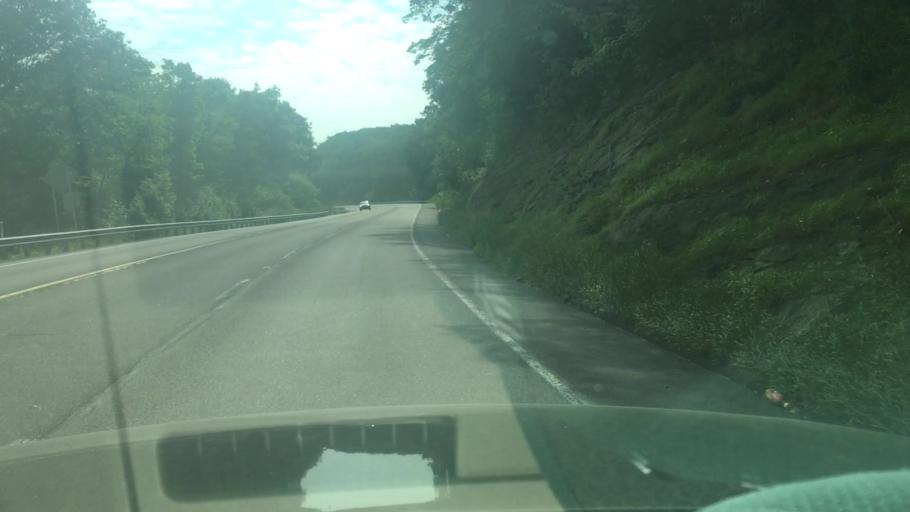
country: US
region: Pennsylvania
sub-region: Northumberland County
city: Elysburg
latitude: 40.8503
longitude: -76.5377
